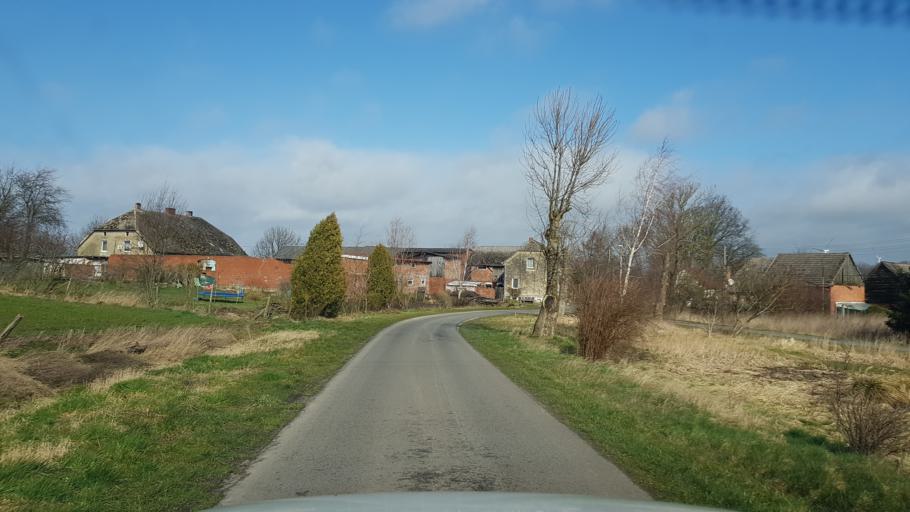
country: PL
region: West Pomeranian Voivodeship
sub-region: Powiat slawienski
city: Slawno
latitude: 54.4799
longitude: 16.6504
